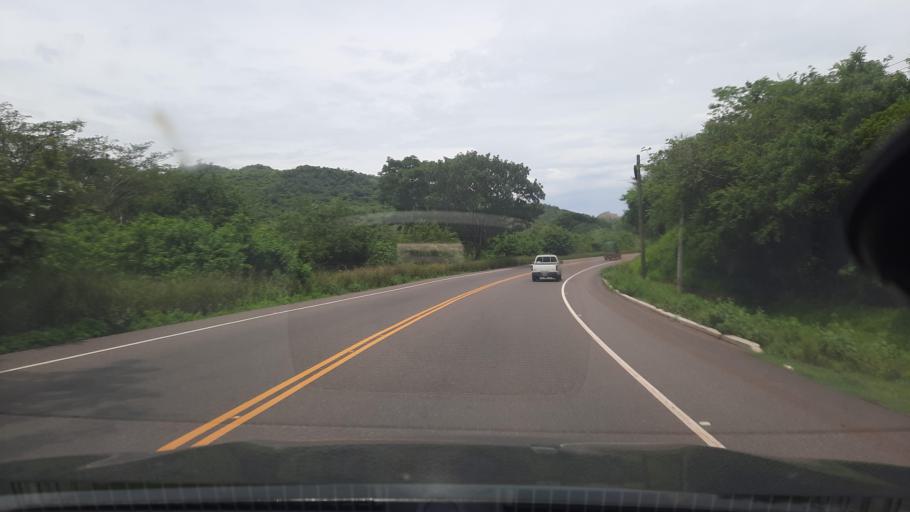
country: HN
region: Valle
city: Langue
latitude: 13.5933
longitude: -87.6985
